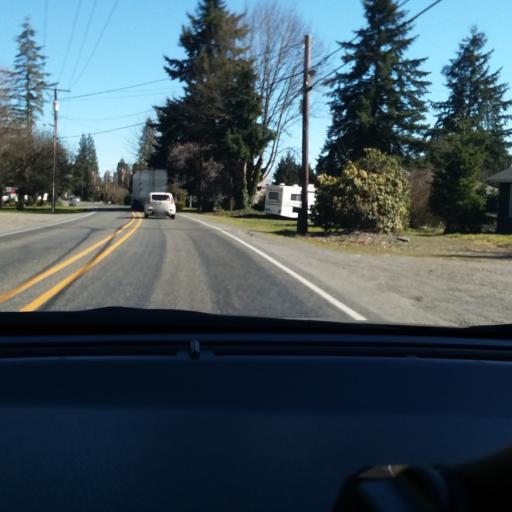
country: US
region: Washington
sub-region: Pierce County
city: North Puyallup
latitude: 47.2065
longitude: -122.2734
